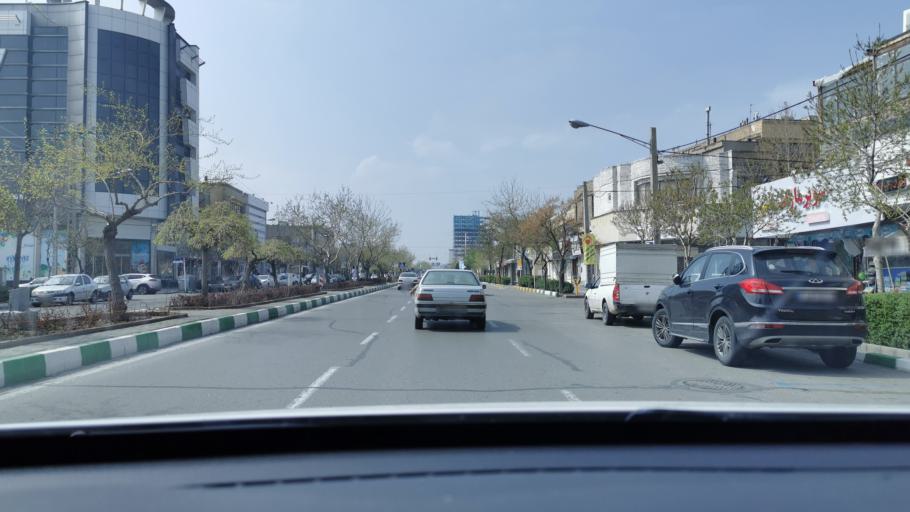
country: IR
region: Razavi Khorasan
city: Mashhad
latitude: 36.3303
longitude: 59.5224
